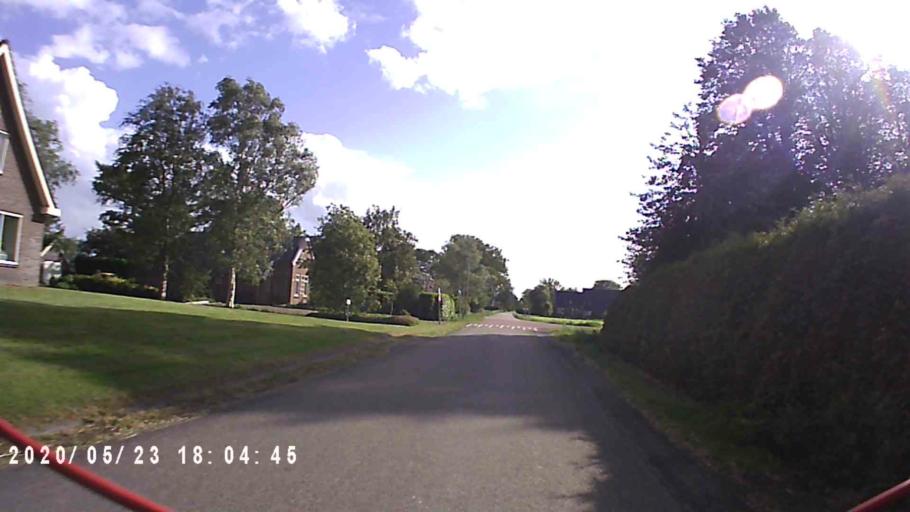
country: NL
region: Groningen
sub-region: Gemeente Slochteren
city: Slochteren
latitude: 53.2424
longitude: 6.7209
